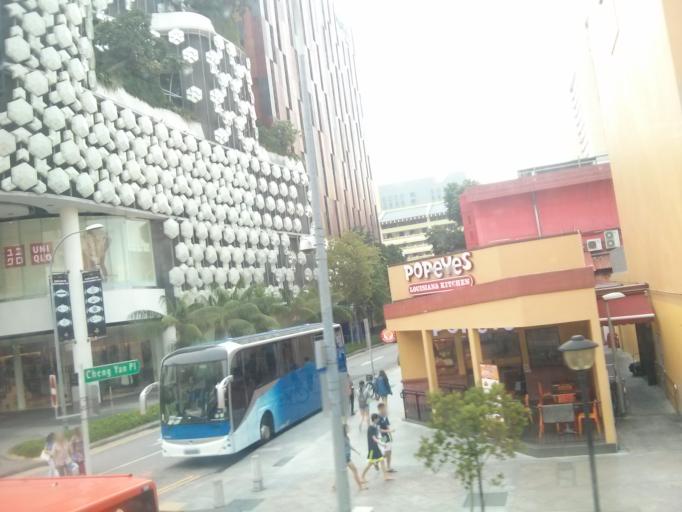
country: SG
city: Singapore
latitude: 1.2998
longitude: 103.8549
